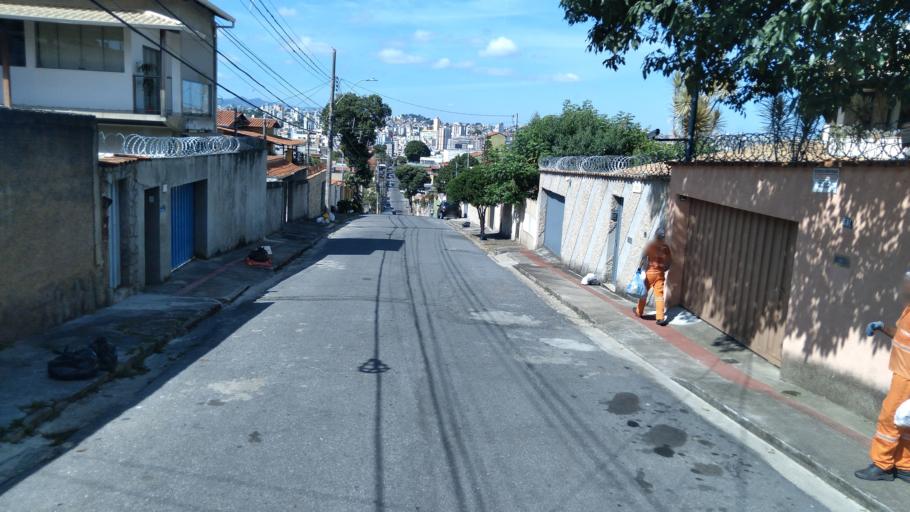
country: BR
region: Minas Gerais
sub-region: Belo Horizonte
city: Belo Horizonte
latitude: -19.8787
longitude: -43.9213
